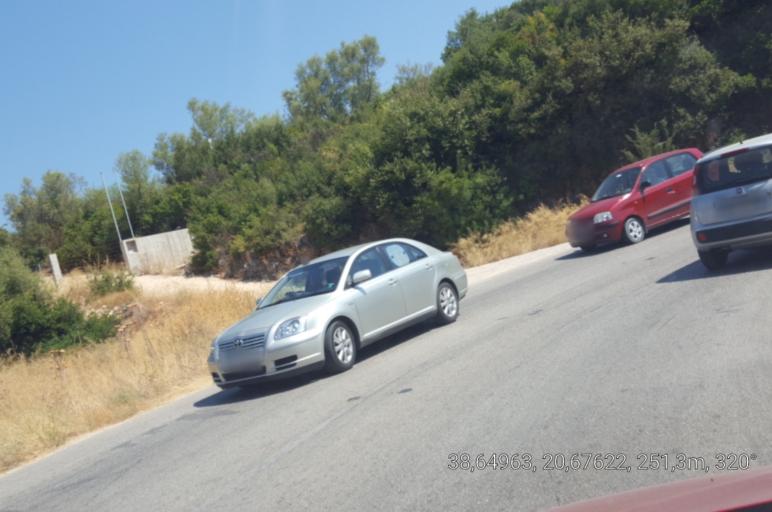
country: GR
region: Ionian Islands
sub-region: Lefkada
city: Nidri
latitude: 38.6494
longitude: 20.6761
